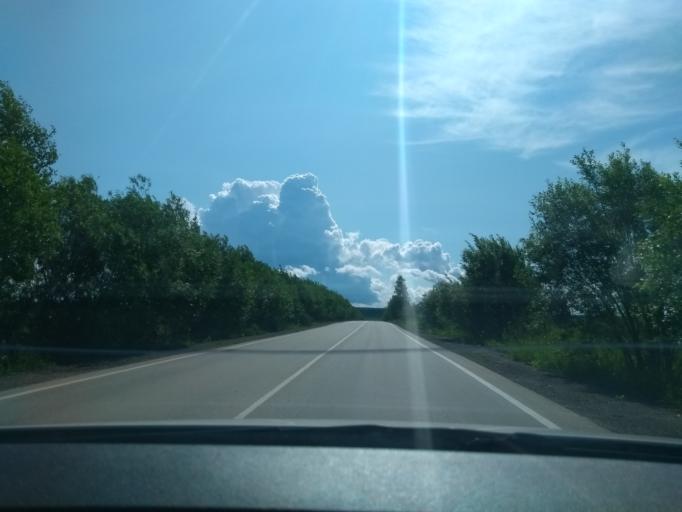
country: RU
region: Perm
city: Bershet'
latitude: 57.8147
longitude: 56.4490
